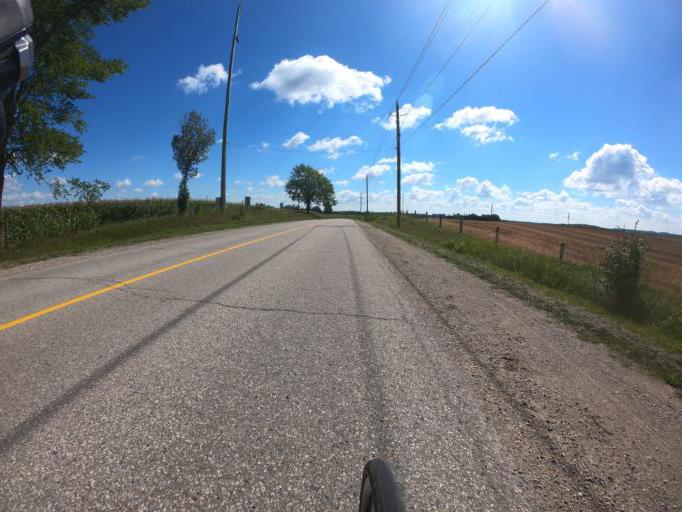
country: CA
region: Ontario
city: Waterloo
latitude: 43.5024
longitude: -80.6243
